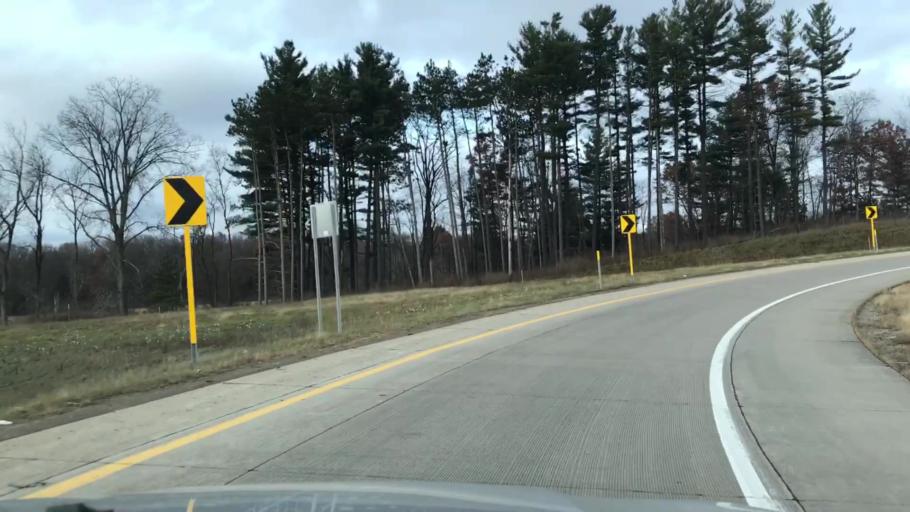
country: US
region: Michigan
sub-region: Oakland County
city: South Lyon
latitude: 42.5223
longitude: -83.6908
